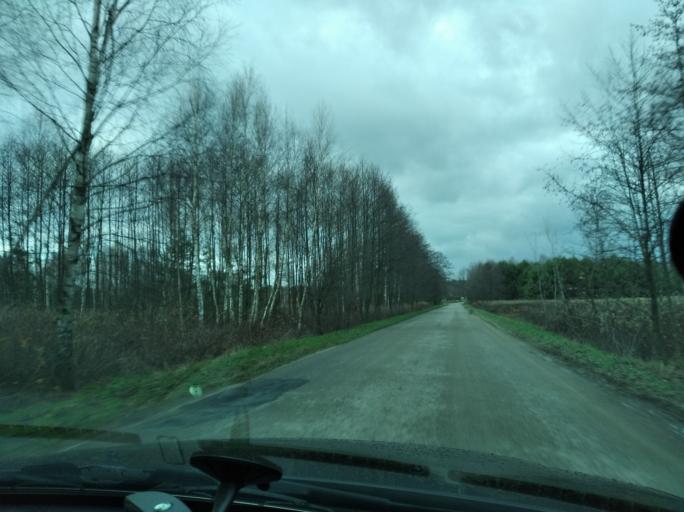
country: PL
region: Subcarpathian Voivodeship
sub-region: Powiat lancucki
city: Zolynia
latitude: 50.1414
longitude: 22.2795
